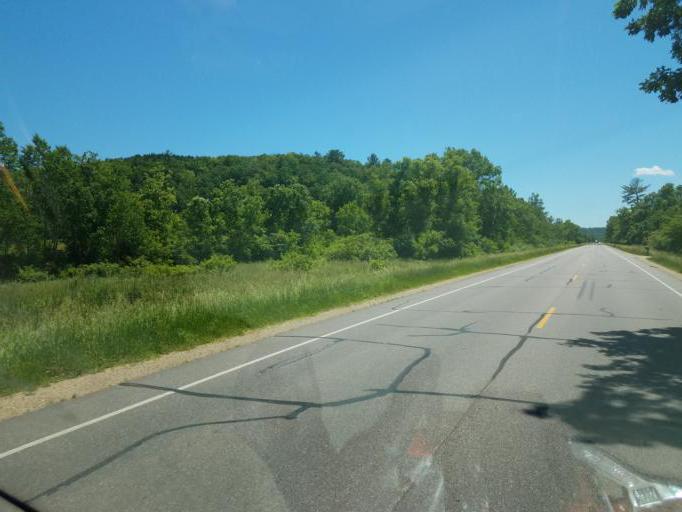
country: US
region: Wisconsin
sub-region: Juneau County
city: Elroy
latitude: 43.6975
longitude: -90.2665
